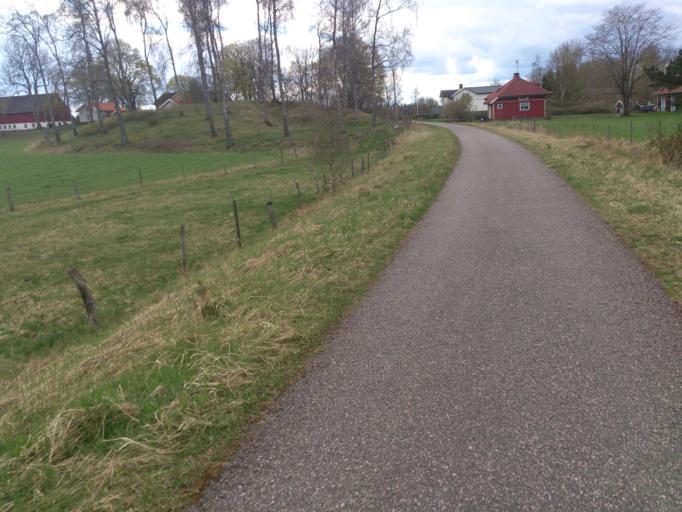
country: SE
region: Vaestra Goetaland
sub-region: Falkopings Kommun
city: Falkoeping
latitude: 57.9823
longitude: 13.5249
